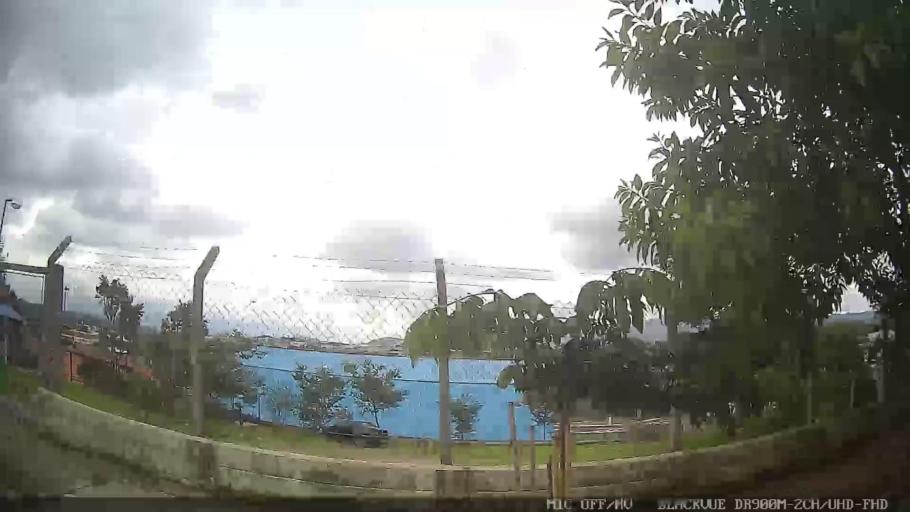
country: BR
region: Sao Paulo
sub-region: Atibaia
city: Atibaia
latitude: -23.1187
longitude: -46.5819
